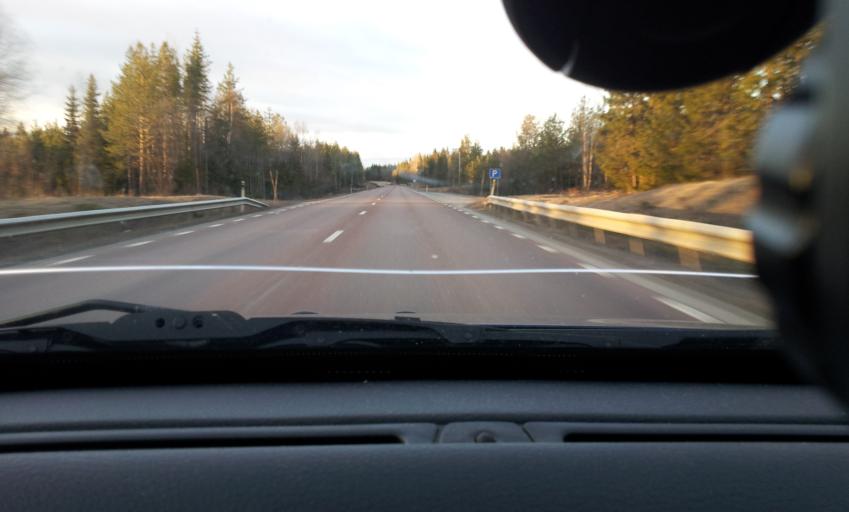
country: SE
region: Jaemtland
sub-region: Bergs Kommun
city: Hoverberg
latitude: 62.9352
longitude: 14.5404
